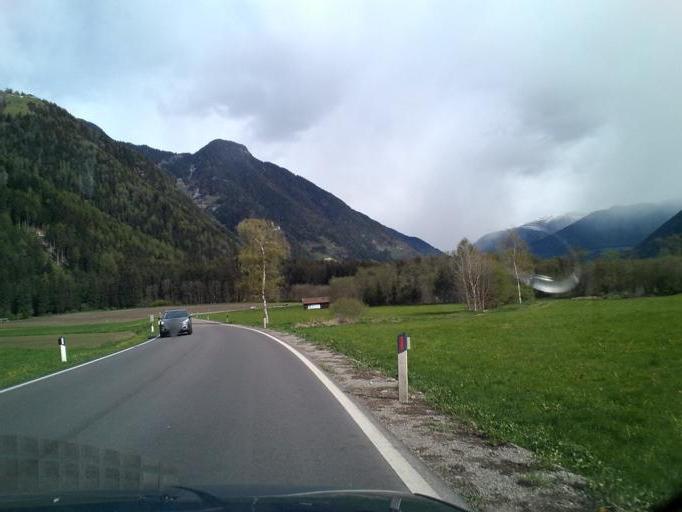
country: IT
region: Trentino-Alto Adige
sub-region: Bolzano
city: Gais
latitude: 46.8500
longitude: 11.9490
